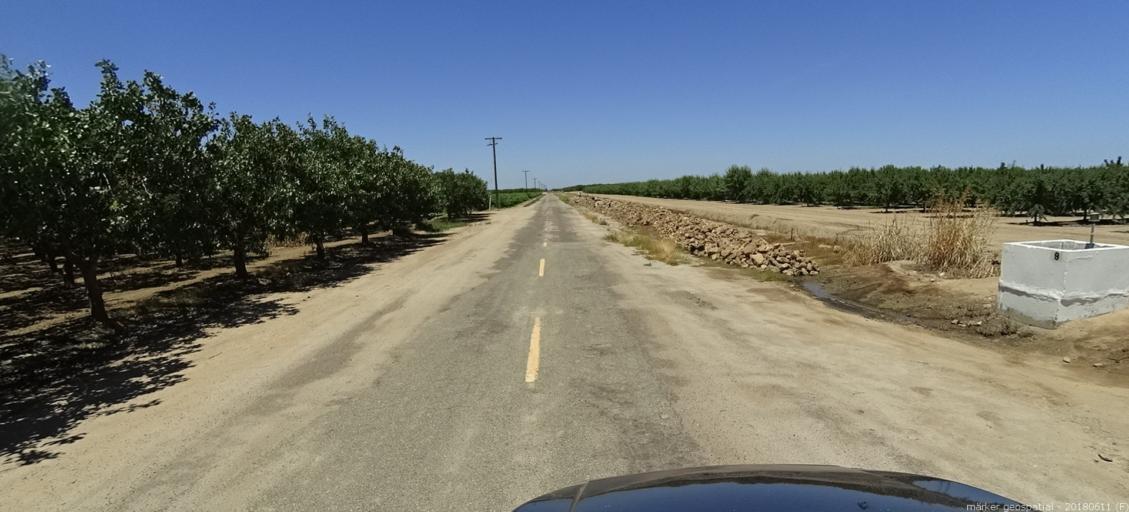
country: US
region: California
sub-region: Madera County
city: Fairmead
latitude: 37.0256
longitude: -120.2152
